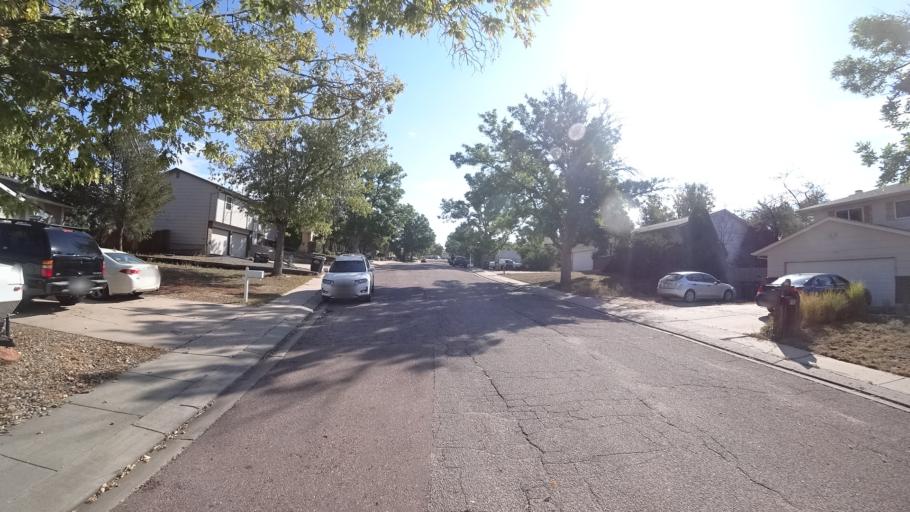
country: US
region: Colorado
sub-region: El Paso County
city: Cimarron Hills
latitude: 38.8820
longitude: -104.7323
